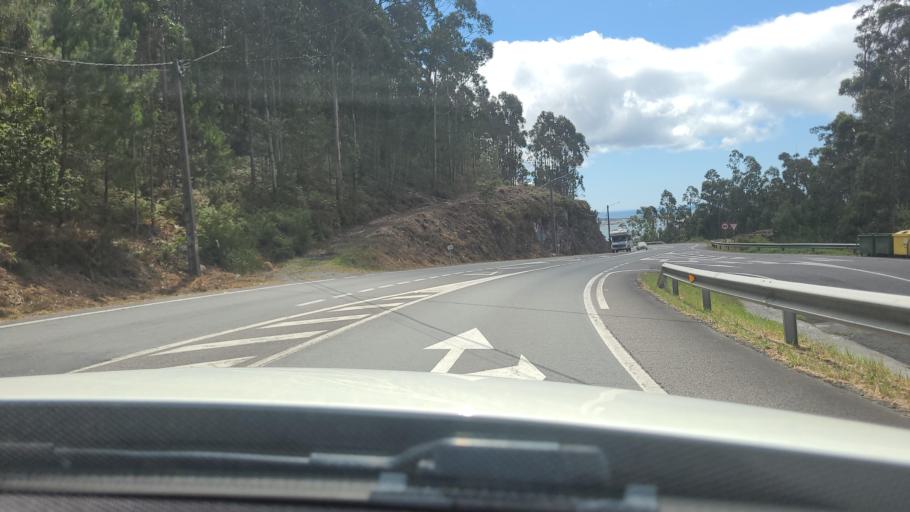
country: ES
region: Galicia
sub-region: Provincia da Coruna
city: Corcubion
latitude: 42.9155
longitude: -9.1455
